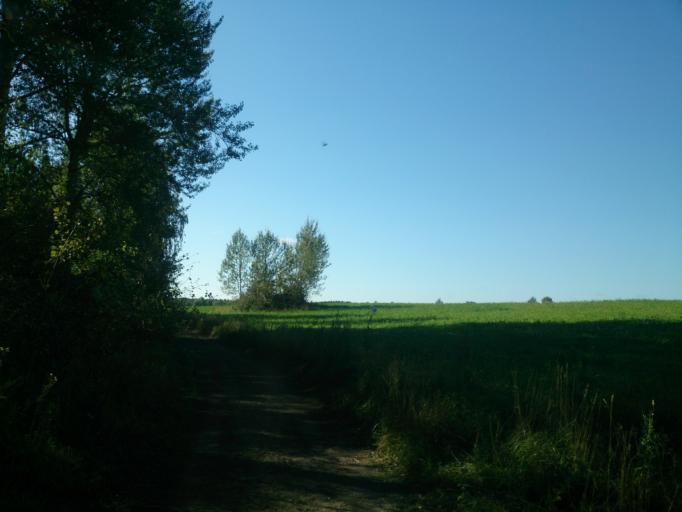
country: SE
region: OEstergoetland
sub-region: Atvidabergs Kommun
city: Atvidaberg
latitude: 58.2237
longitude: 15.9755
